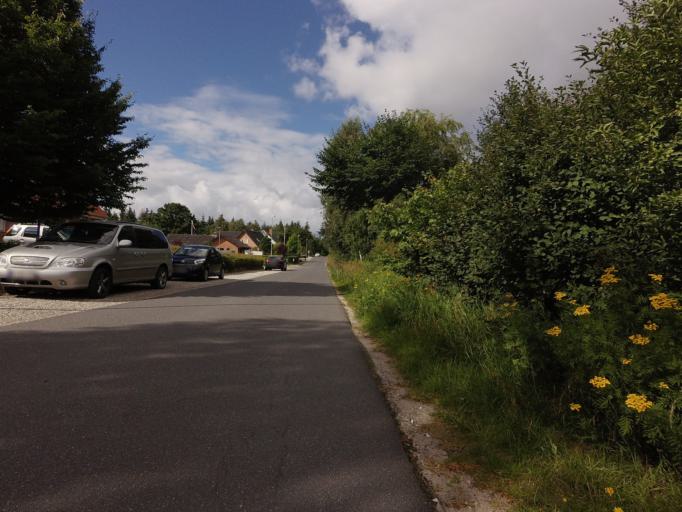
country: DK
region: Central Jutland
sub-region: Silkeborg Kommune
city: Svejbaek
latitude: 56.1814
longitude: 9.6460
